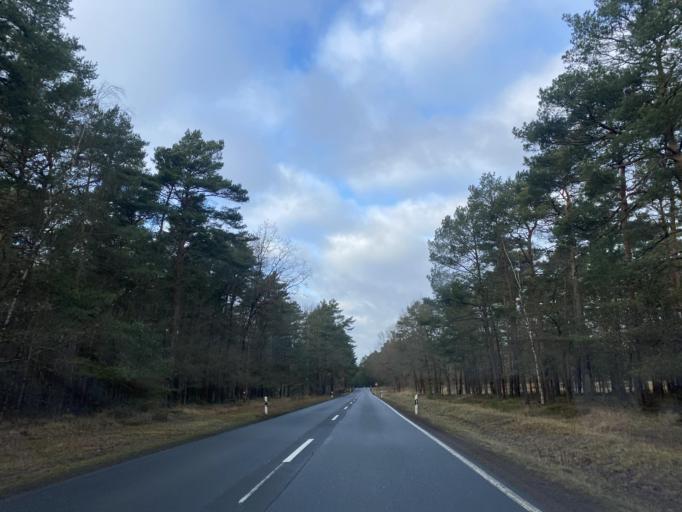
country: DE
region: Saxony
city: Rietschen
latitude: 51.4853
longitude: 14.8437
